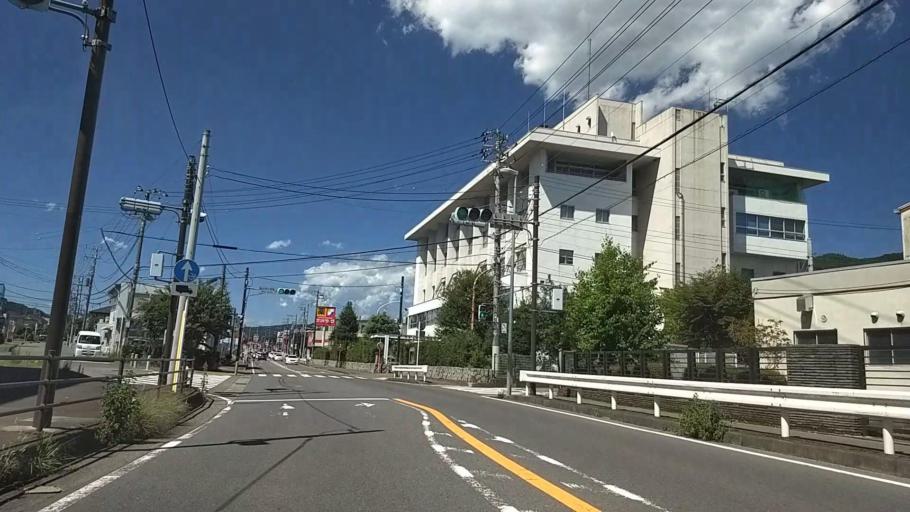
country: JP
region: Tokyo
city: Hachioji
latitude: 35.5867
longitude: 139.2566
